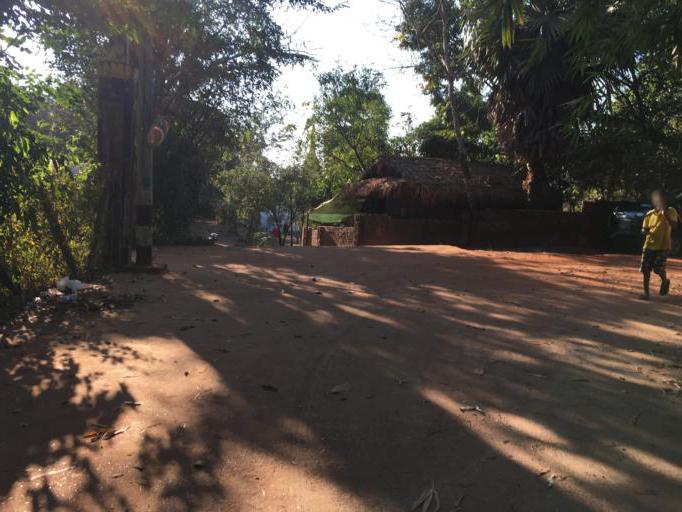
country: MM
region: Mon
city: Mawlamyine
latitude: 16.4490
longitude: 97.6362
